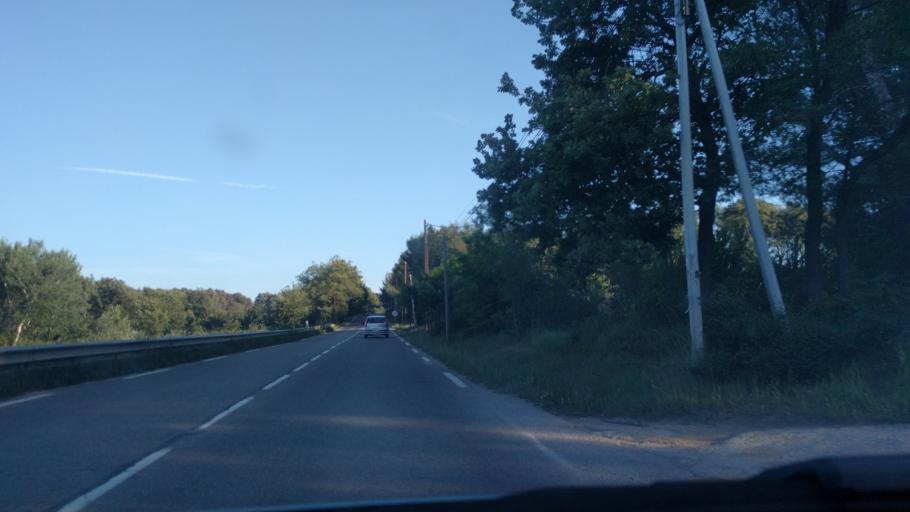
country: FR
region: Provence-Alpes-Cote d'Azur
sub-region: Departement des Bouches-du-Rhone
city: Venelles
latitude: 43.6275
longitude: 5.4897
